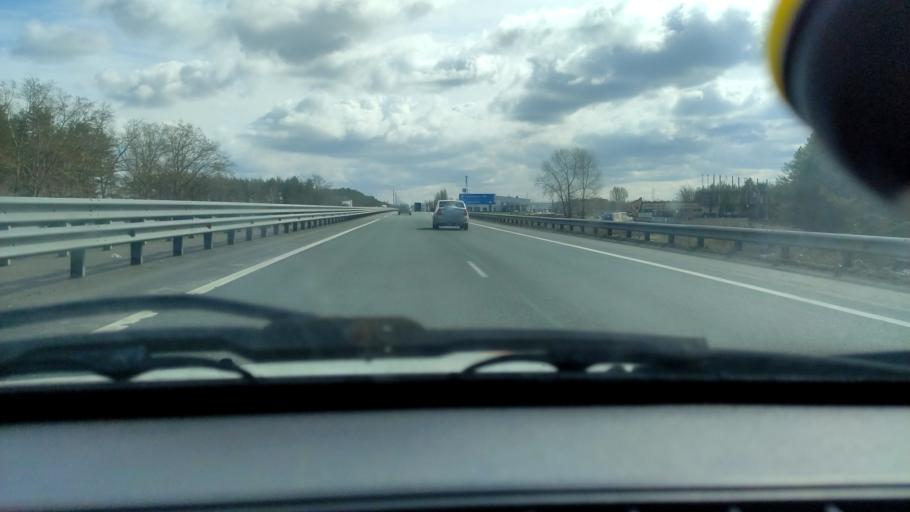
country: RU
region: Samara
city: Zhigulevsk
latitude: 53.5130
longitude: 49.5876
